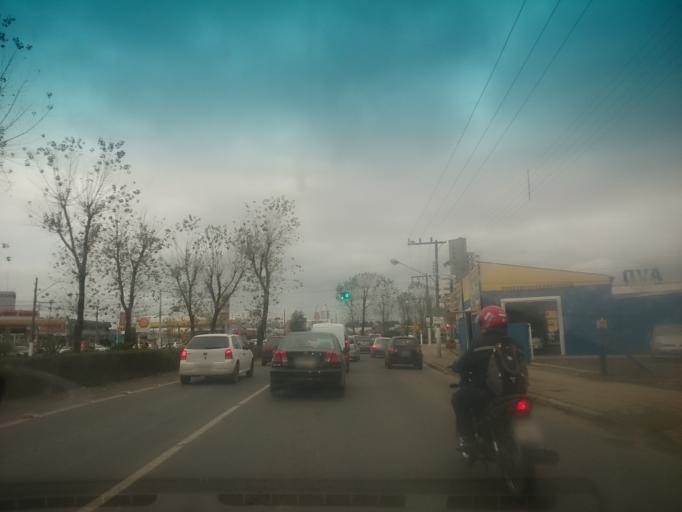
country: BR
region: Santa Catarina
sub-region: Lages
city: Lages
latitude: -27.8072
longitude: -50.3208
